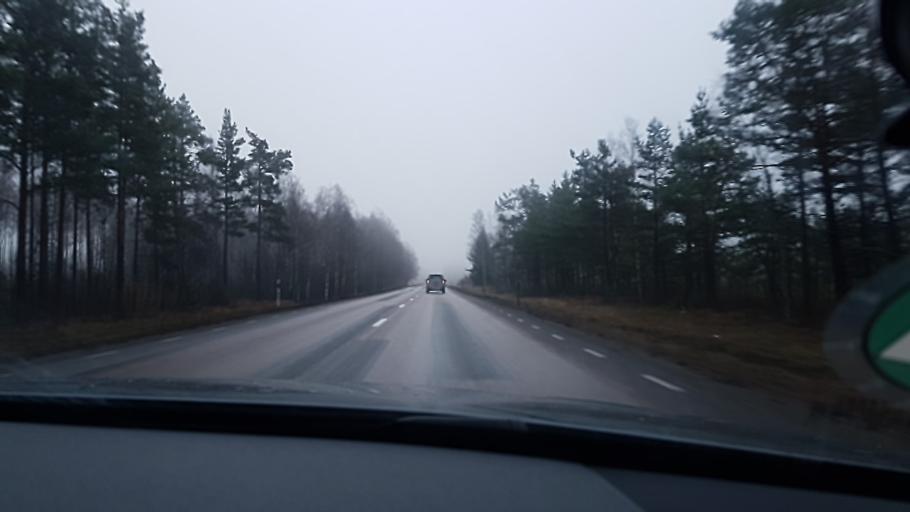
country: SE
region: Vaermland
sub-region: Kristinehamns Kommun
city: Kristinehamn
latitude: 59.2719
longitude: 14.1598
